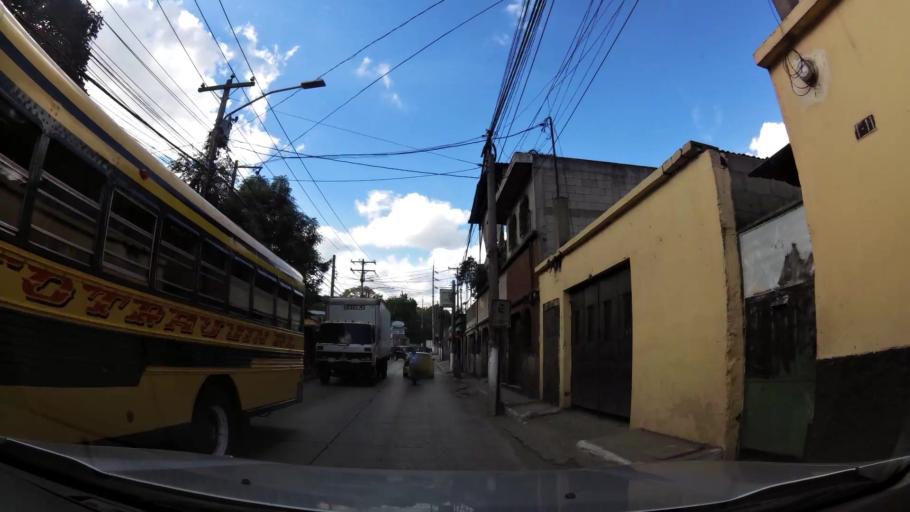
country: GT
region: Guatemala
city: Villa Nueva
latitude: 14.5276
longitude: -90.5939
